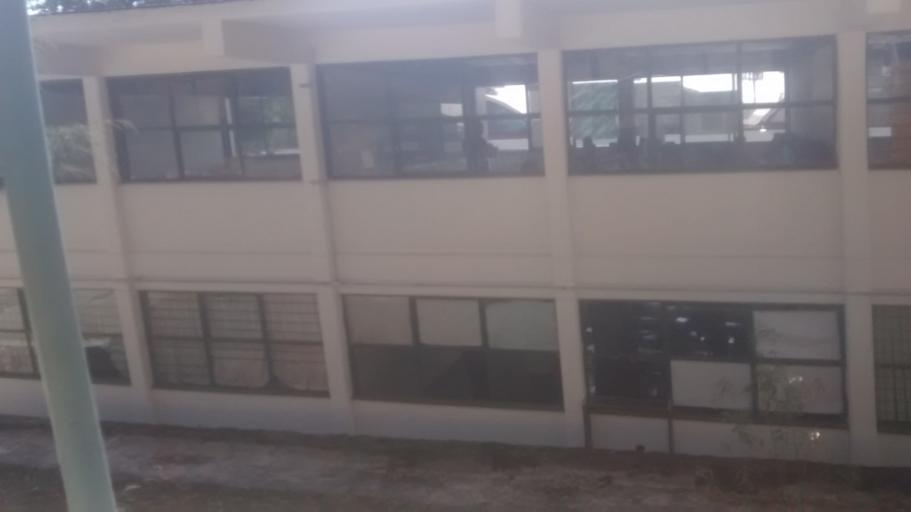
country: MX
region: Mexico
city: San Buenaventura
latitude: 19.2828
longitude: -99.6771
